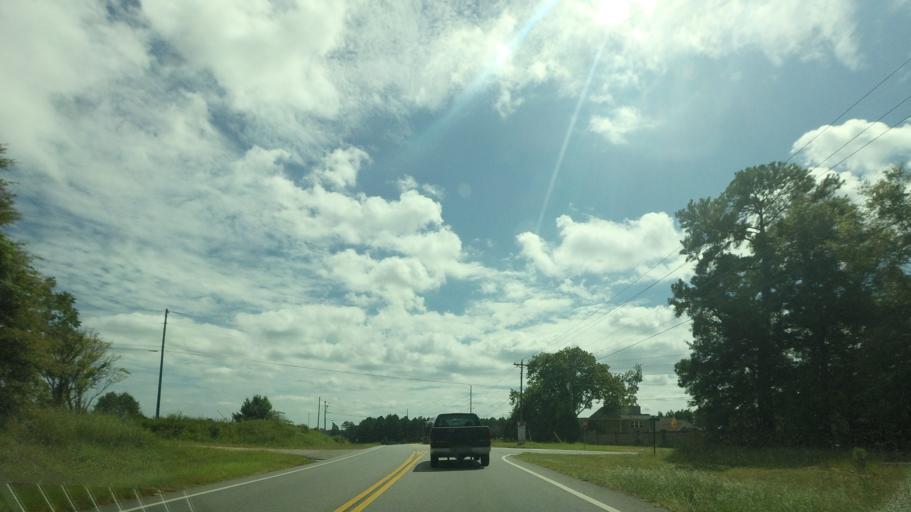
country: US
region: Georgia
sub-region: Houston County
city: Robins Air Force Base
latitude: 32.5441
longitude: -83.5906
